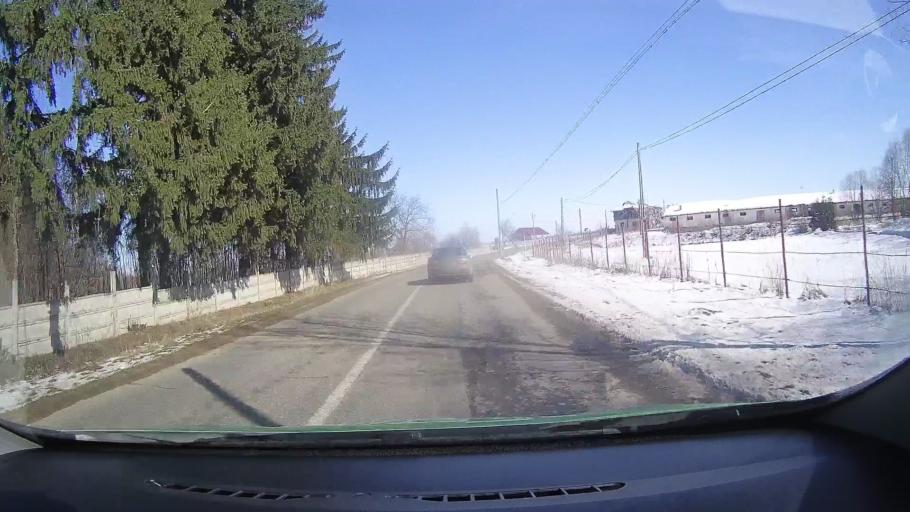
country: RO
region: Brasov
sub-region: Comuna Recea
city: Recea
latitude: 45.7300
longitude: 24.9095
